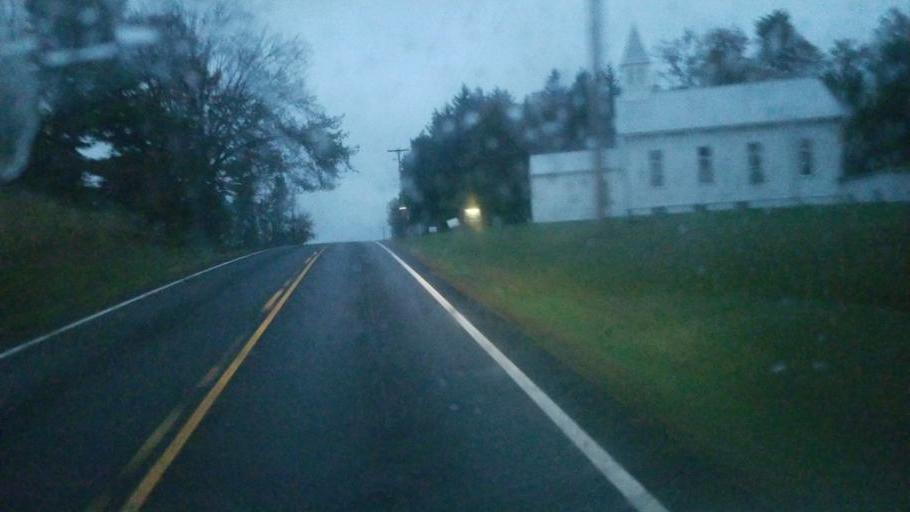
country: US
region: Ohio
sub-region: Richland County
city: Lexington
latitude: 40.6077
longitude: -82.5875
